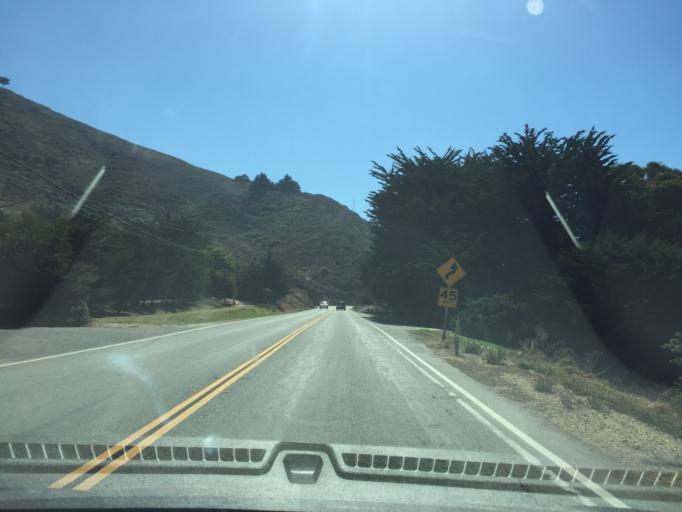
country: US
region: California
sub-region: Monterey County
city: Carmel-by-the-Sea
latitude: 36.4143
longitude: -121.9143
